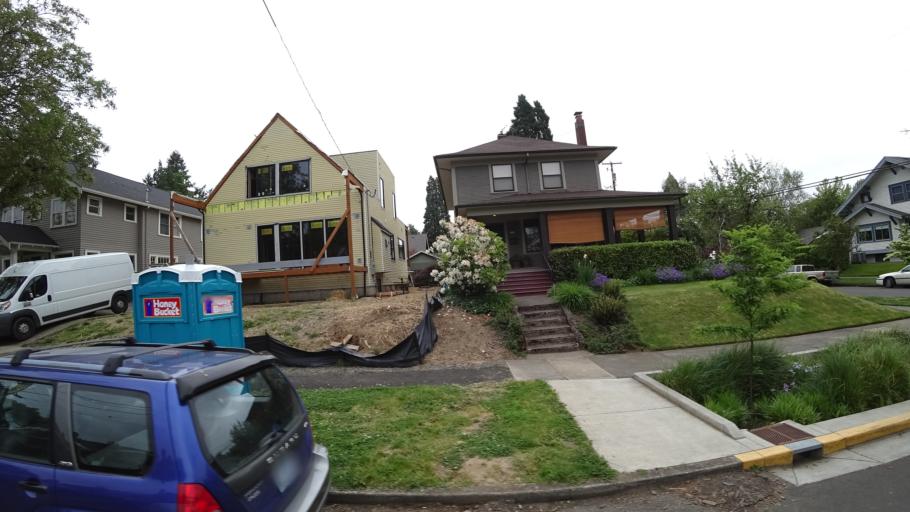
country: US
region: Oregon
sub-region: Multnomah County
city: Portland
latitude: 45.5408
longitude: -122.6130
